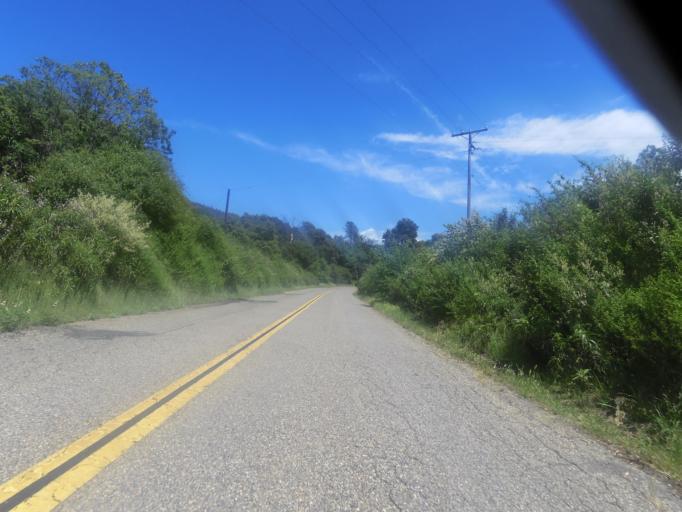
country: US
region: California
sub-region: Mariposa County
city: Midpines
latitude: 37.5095
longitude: -119.8772
